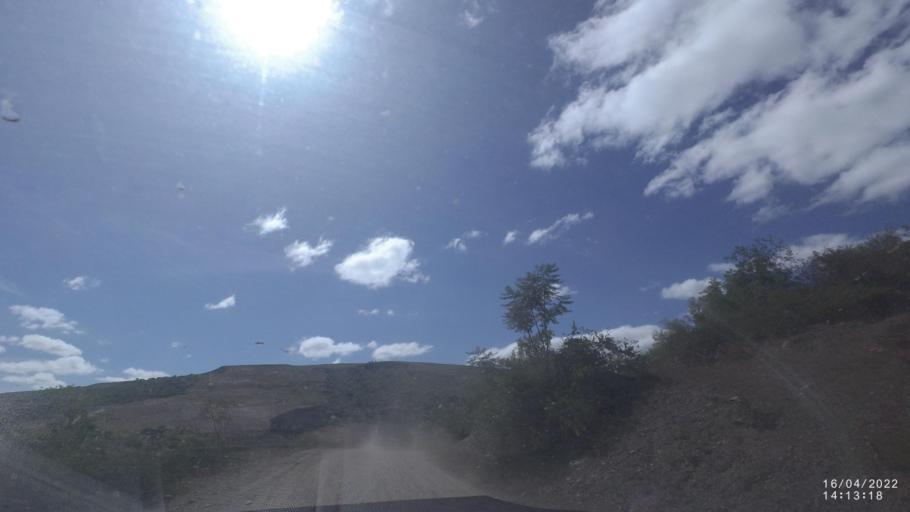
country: BO
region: Cochabamba
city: Mizque
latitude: -18.0602
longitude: -65.5096
